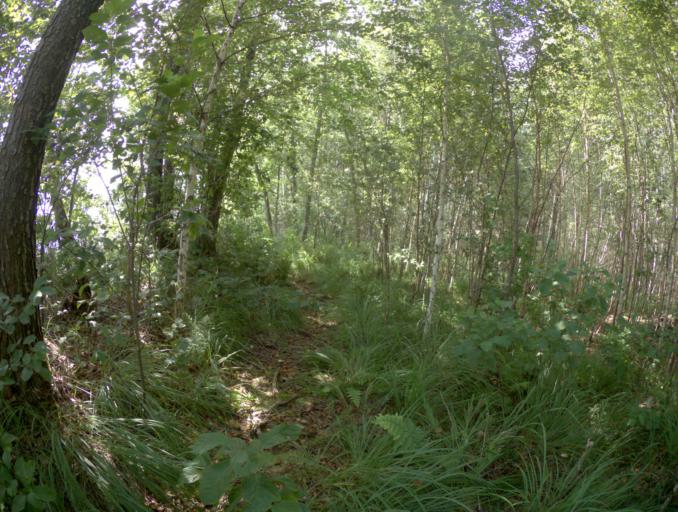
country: RU
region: Vladimir
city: Vorsha
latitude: 55.9476
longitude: 40.1926
